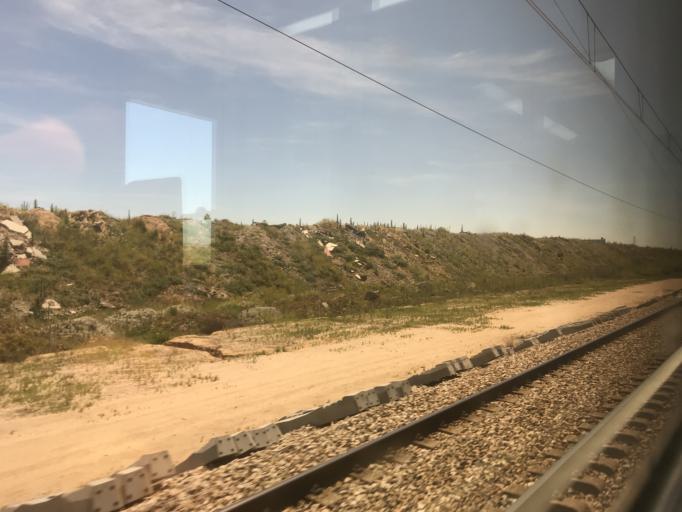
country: ES
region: Madrid
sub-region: Provincia de Madrid
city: Getafe
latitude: 40.2900
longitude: -3.7053
